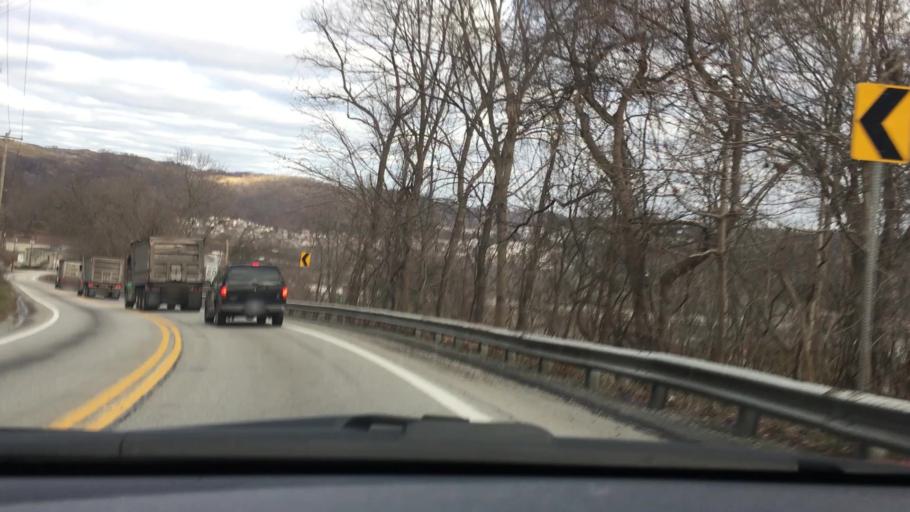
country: US
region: Pennsylvania
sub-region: Westmoreland County
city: Trafford
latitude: 40.3884
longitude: -79.7735
